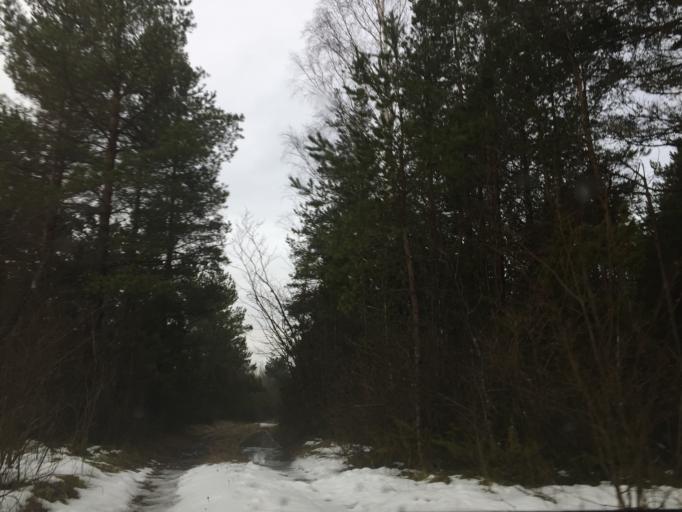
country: EE
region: Saare
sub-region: Orissaare vald
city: Orissaare
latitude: 58.6101
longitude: 22.9546
